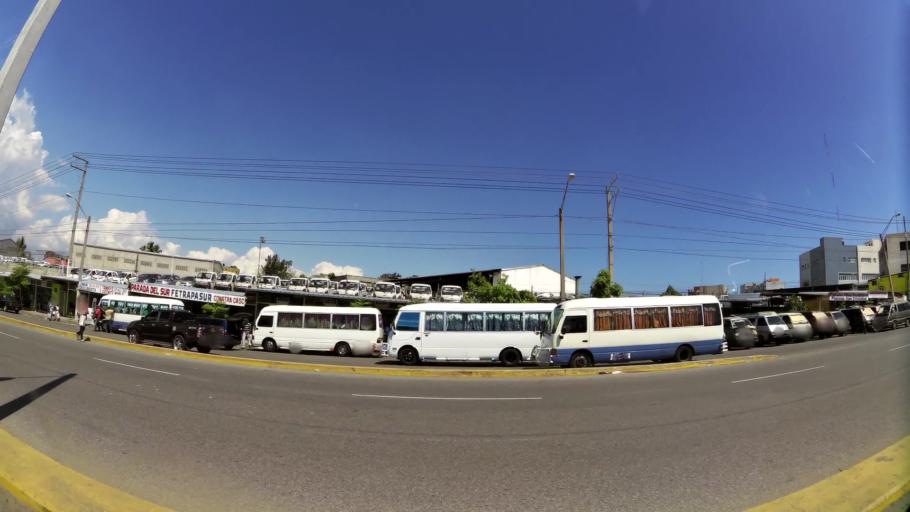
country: DO
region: Nacional
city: Bella Vista
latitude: 18.4526
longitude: -69.9801
